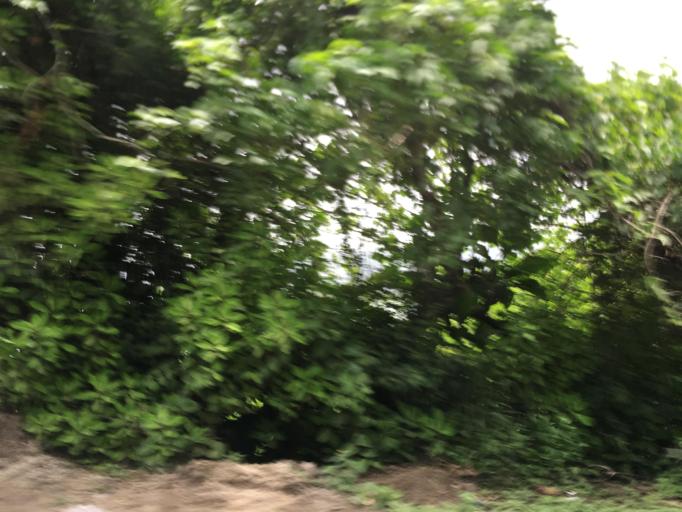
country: GT
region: Guatemala
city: Villa Canales
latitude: 14.4581
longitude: -90.5749
